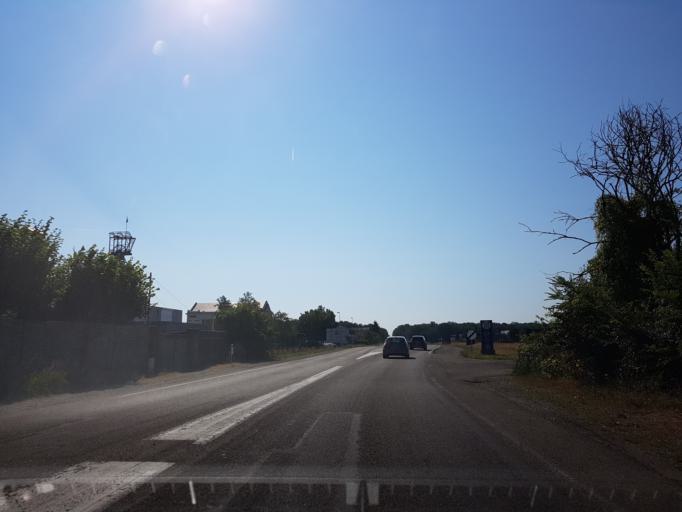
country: FR
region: Alsace
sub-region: Departement du Haut-Rhin
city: Bollwiller
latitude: 47.8480
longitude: 7.2792
